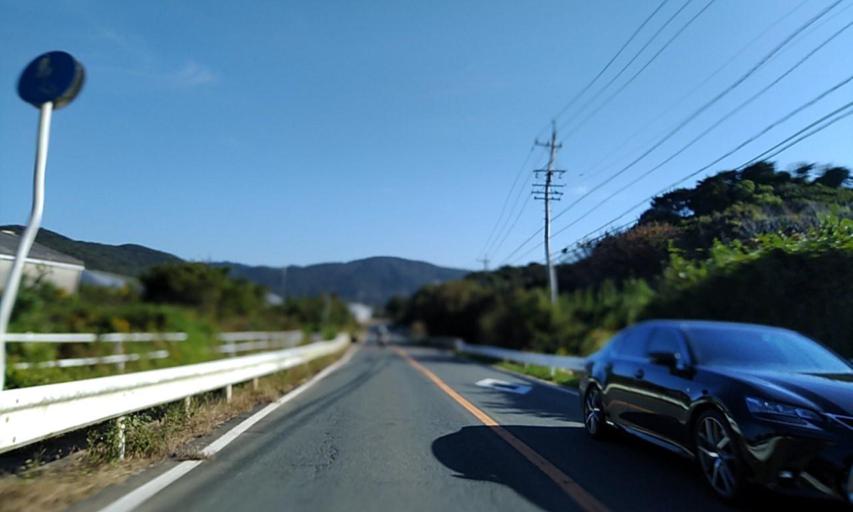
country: JP
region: Aichi
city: Tahara
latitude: 34.5908
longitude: 137.1119
